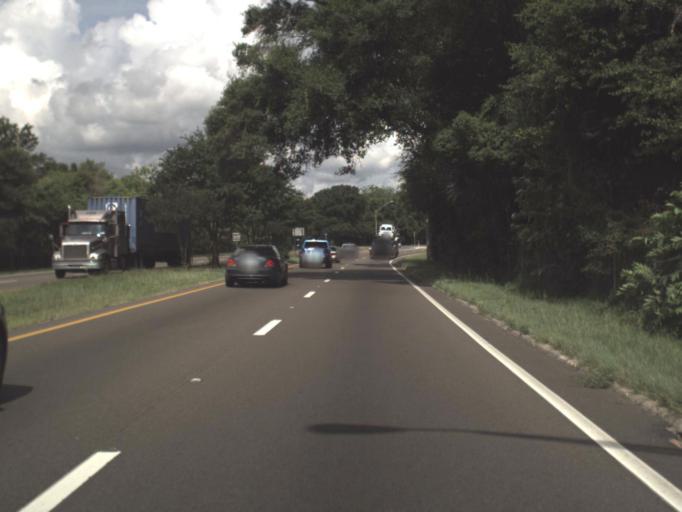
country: US
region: Florida
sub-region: Duval County
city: Jacksonville
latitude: 30.3556
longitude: -81.6786
